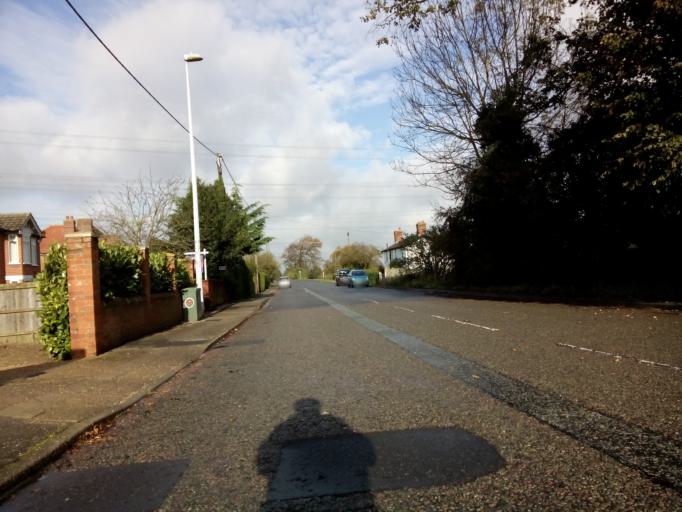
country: GB
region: England
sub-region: Suffolk
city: Bramford
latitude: 52.0872
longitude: 1.1227
